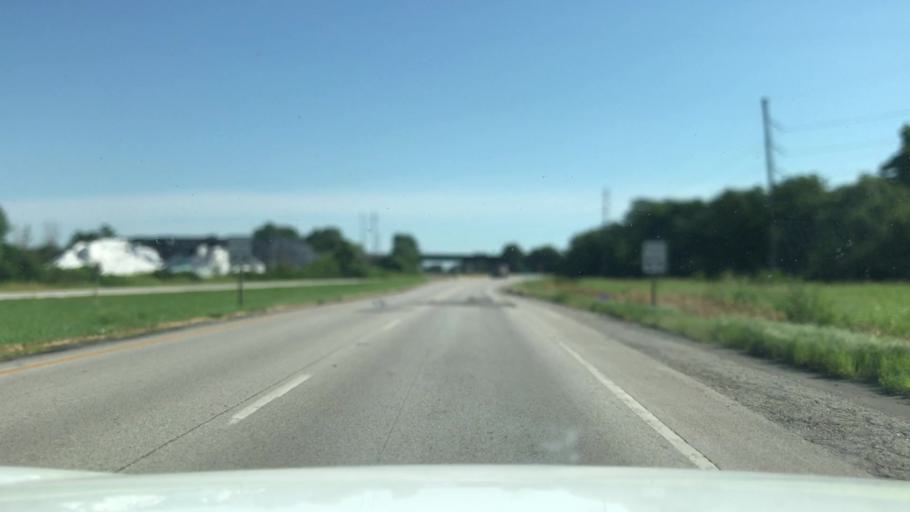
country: US
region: Illinois
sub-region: Madison County
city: Venice
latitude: 38.6731
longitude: -90.1753
